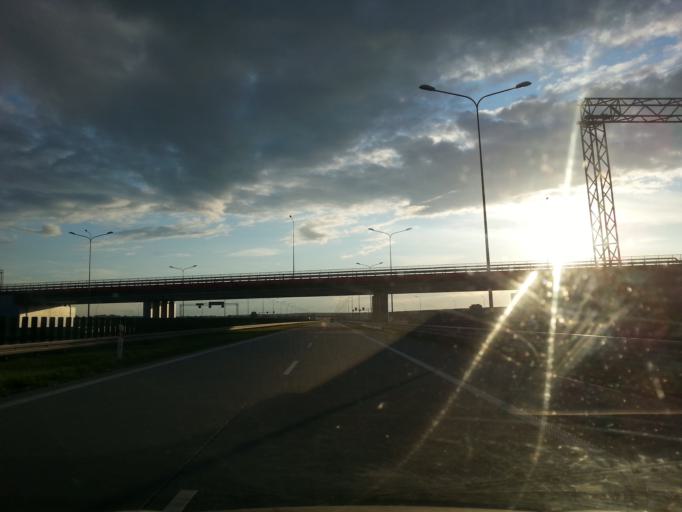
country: PL
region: Lodz Voivodeship
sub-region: Powiat wieruszowski
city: Walichnowy
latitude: 51.3161
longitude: 18.3880
